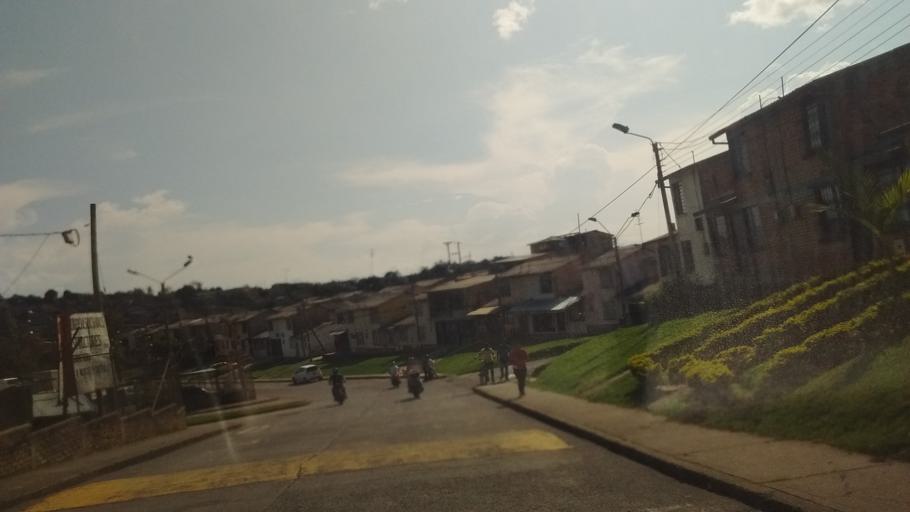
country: CO
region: Cauca
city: Popayan
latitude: 2.4517
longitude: -76.6335
